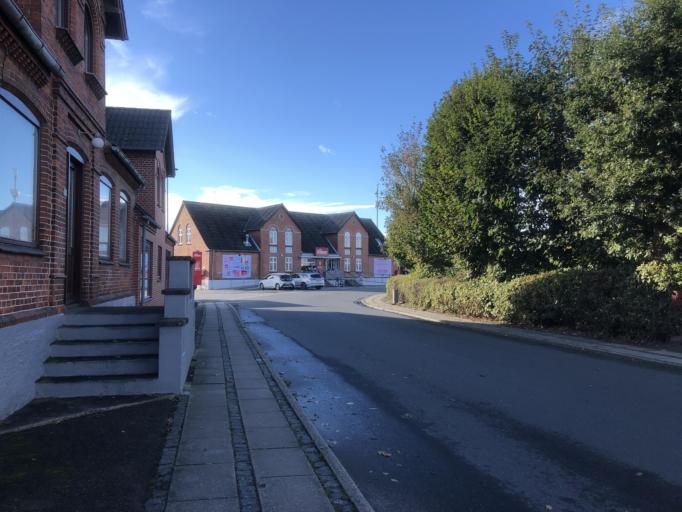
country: DK
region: South Denmark
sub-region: AEro Kommune
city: Marstal
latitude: 54.7497
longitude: 10.6729
